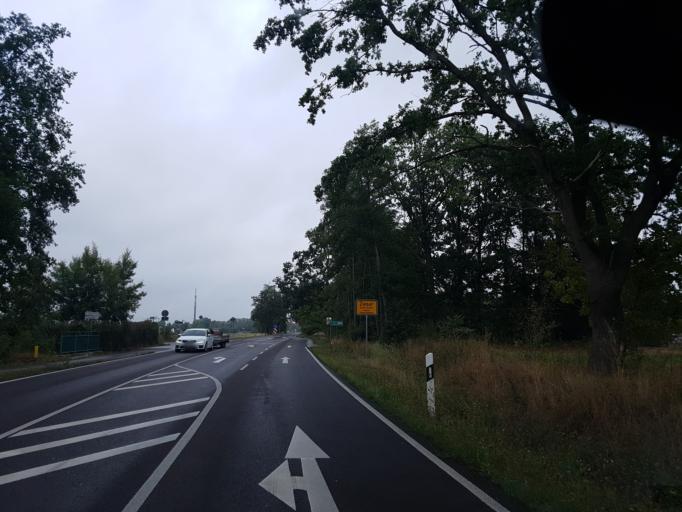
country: DE
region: Brandenburg
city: Ziesar
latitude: 52.2580
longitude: 12.2911
